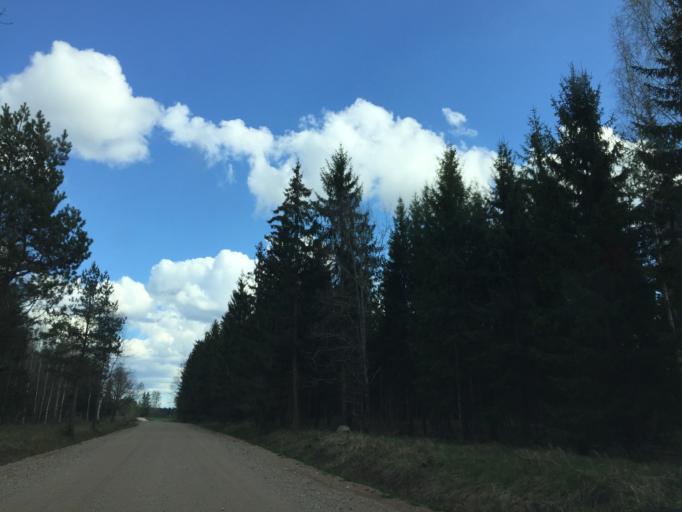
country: LV
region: Beverina
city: Murmuiza
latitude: 57.4613
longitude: 25.5129
